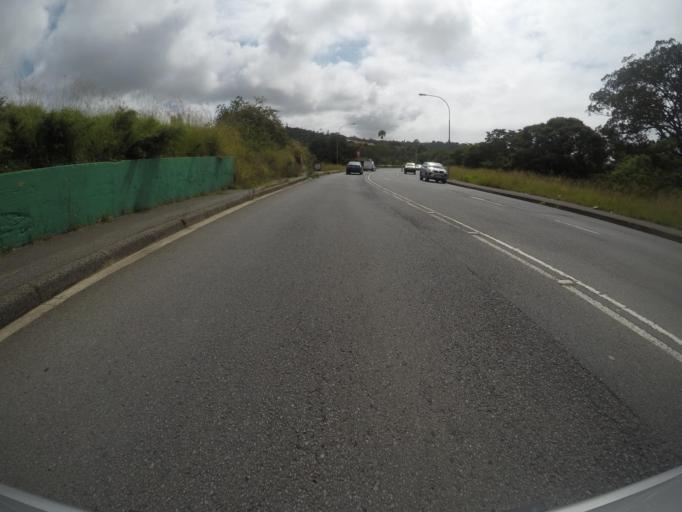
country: ZA
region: Eastern Cape
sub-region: Buffalo City Metropolitan Municipality
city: East London
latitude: -32.9742
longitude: 27.9232
